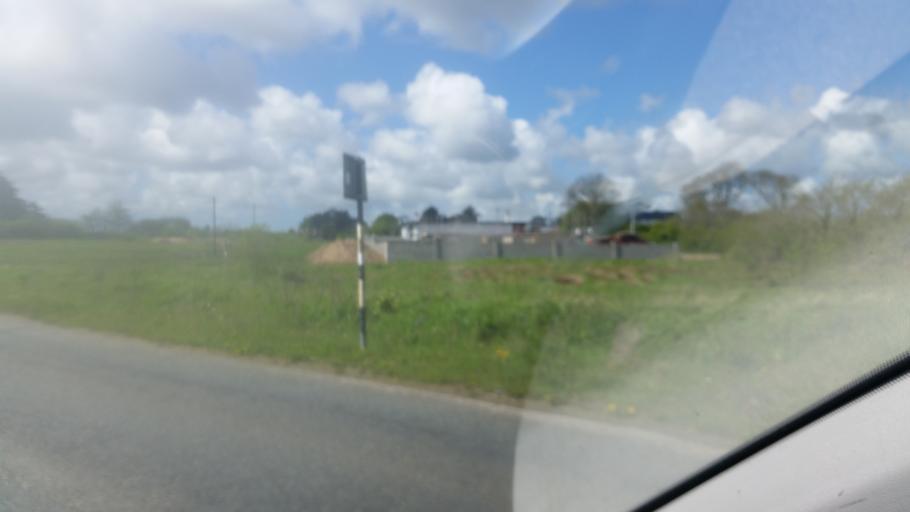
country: IE
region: Leinster
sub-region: Loch Garman
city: Loch Garman
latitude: 52.3538
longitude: -6.4539
